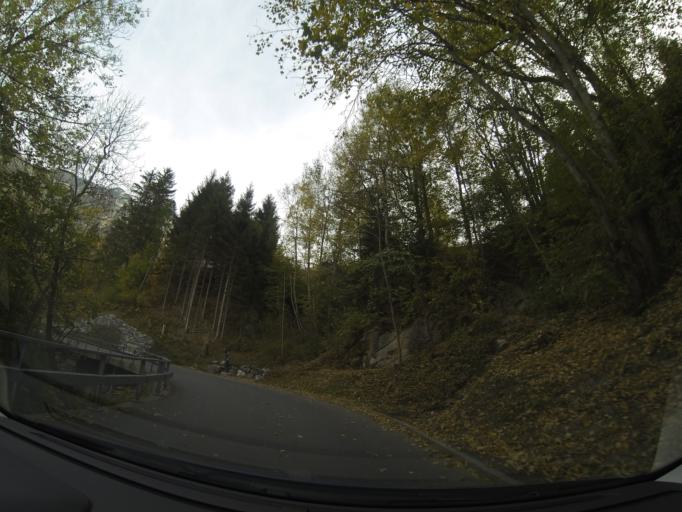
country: CH
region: Saint Gallen
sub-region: Wahlkreis Sarganserland
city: Bad Ragaz
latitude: 46.9549
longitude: 9.4747
